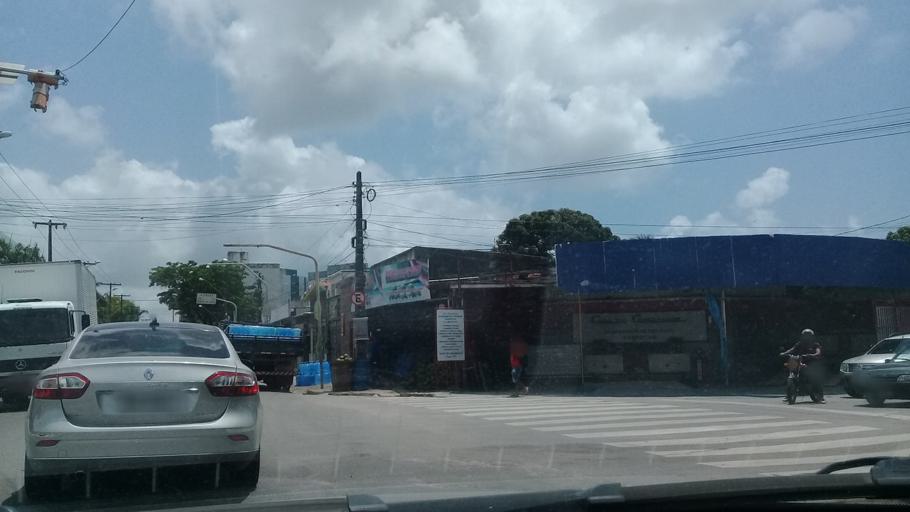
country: BR
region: Pernambuco
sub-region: Recife
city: Recife
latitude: -8.1080
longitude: -34.9161
